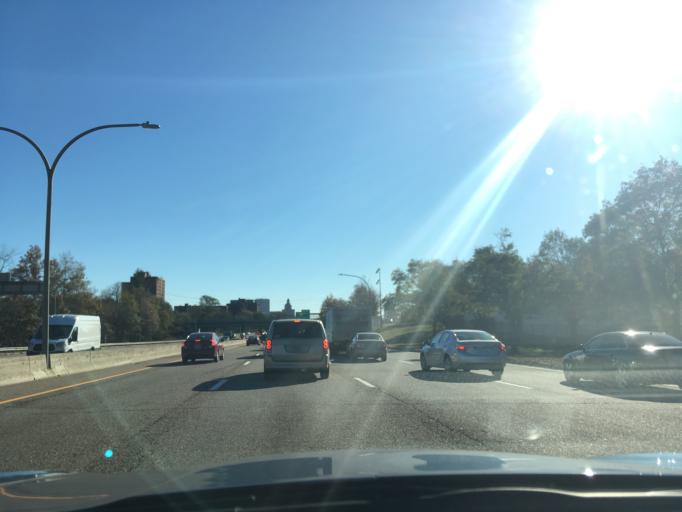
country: US
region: Rhode Island
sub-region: Providence County
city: Providence
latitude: 41.8431
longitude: -71.4111
